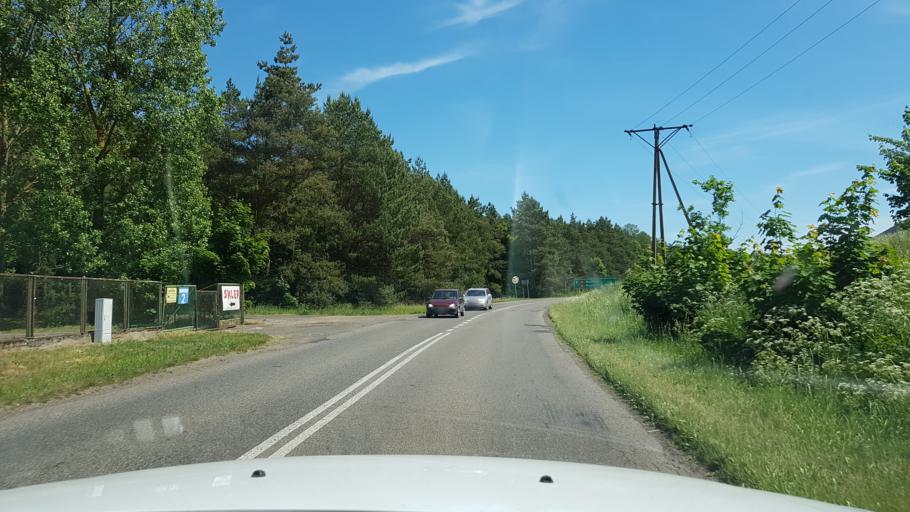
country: PL
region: West Pomeranian Voivodeship
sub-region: Powiat gryfinski
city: Chojna
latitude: 52.9634
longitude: 14.4618
